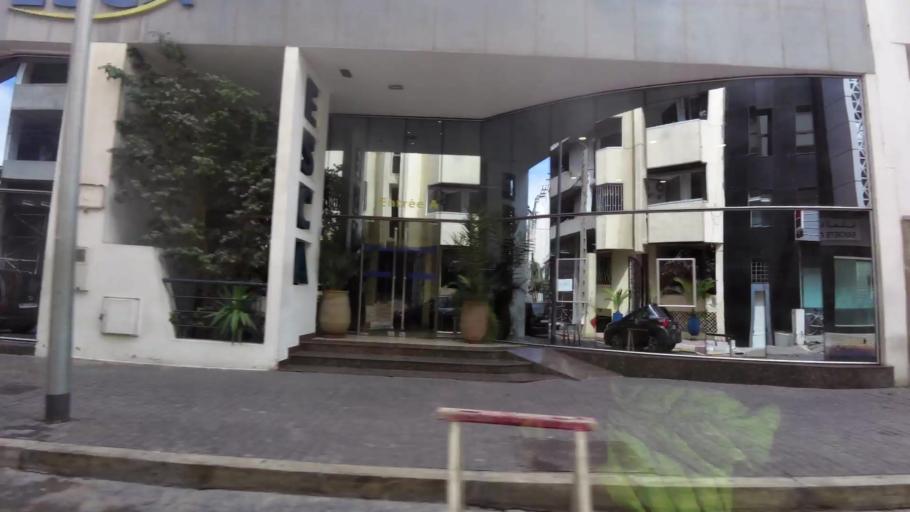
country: MA
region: Grand Casablanca
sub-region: Casablanca
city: Casablanca
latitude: 33.5927
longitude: -7.6276
